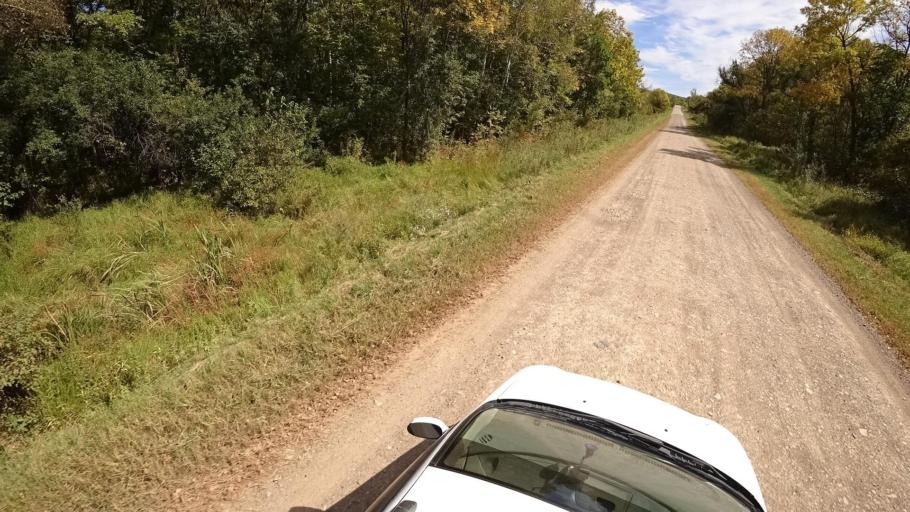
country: RU
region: Primorskiy
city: Yakovlevka
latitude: 44.6588
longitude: 133.7337
